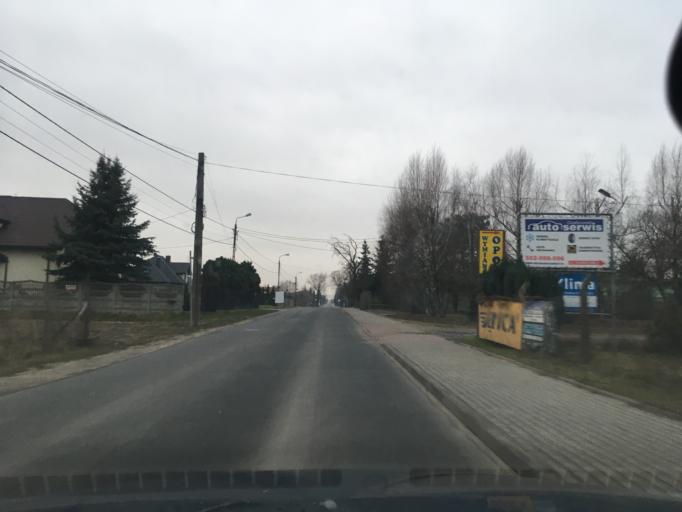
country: PL
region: Masovian Voivodeship
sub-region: Powiat piaseczynski
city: Mysiadlo
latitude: 52.1266
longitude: 20.9797
